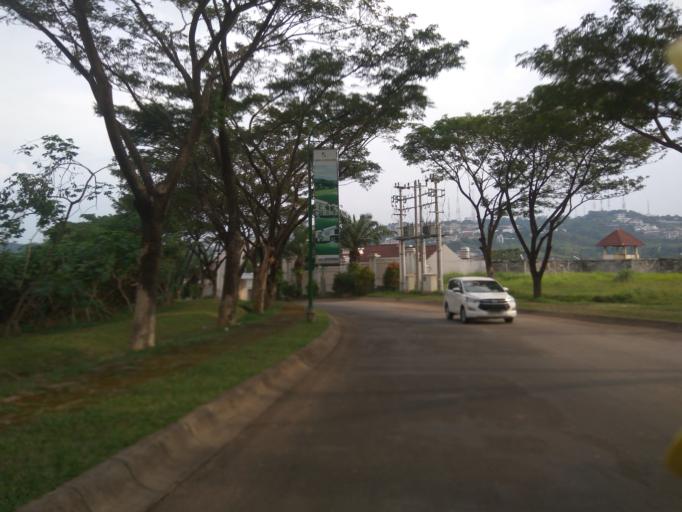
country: ID
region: Central Java
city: Semarang
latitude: -7.0326
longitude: 110.4349
